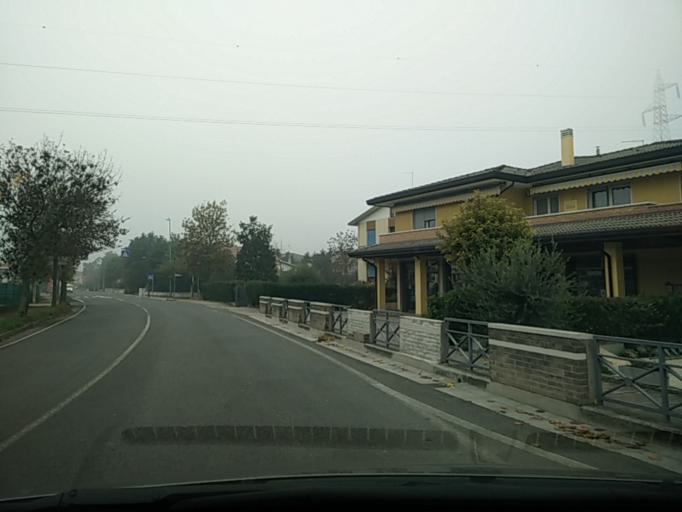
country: IT
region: Veneto
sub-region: Provincia di Venezia
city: Salzano
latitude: 45.5191
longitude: 12.1120
